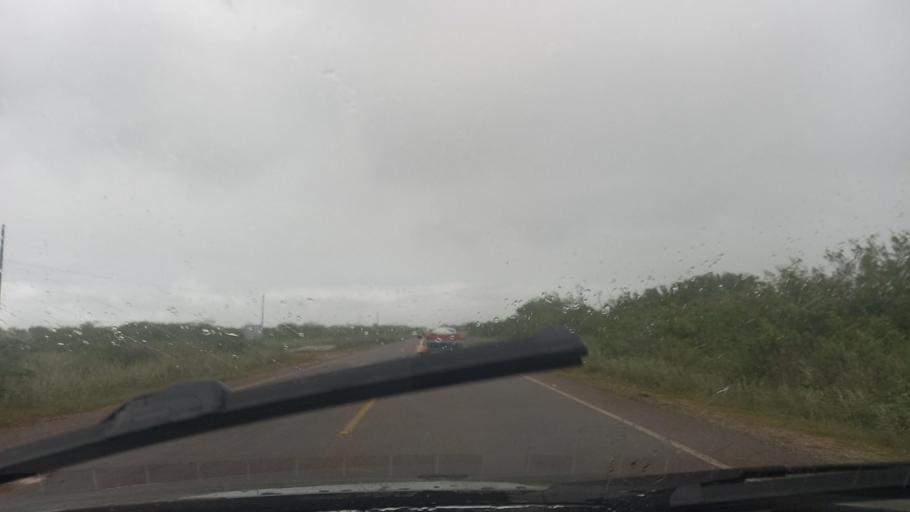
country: BR
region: Bahia
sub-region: Paulo Afonso
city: Paulo Afonso
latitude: -9.3489
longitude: -38.2796
